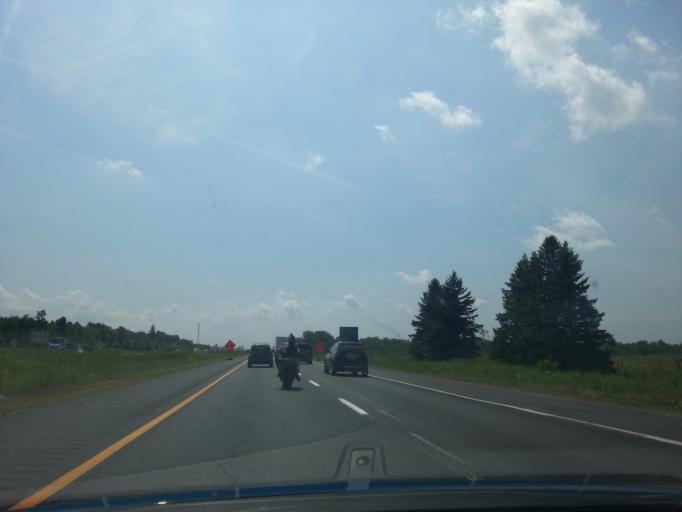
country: CA
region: Quebec
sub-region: Mauricie
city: Saint-Germain-de-Grantham
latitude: 45.8711
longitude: -72.5613
